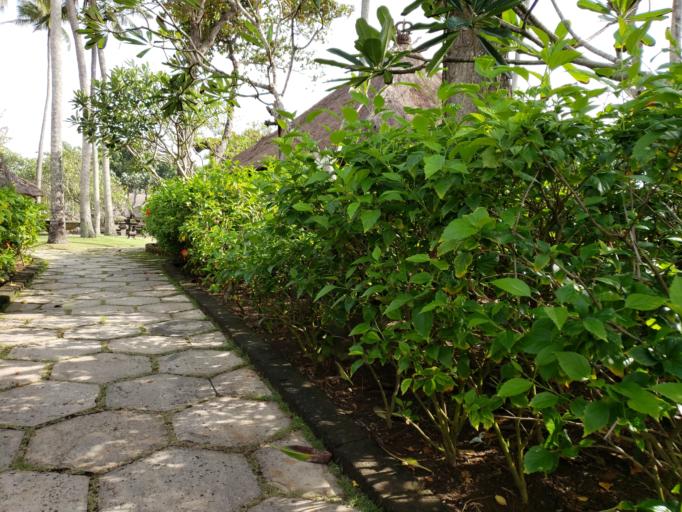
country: ID
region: Bali
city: Kuta
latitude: -8.6887
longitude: 115.1561
